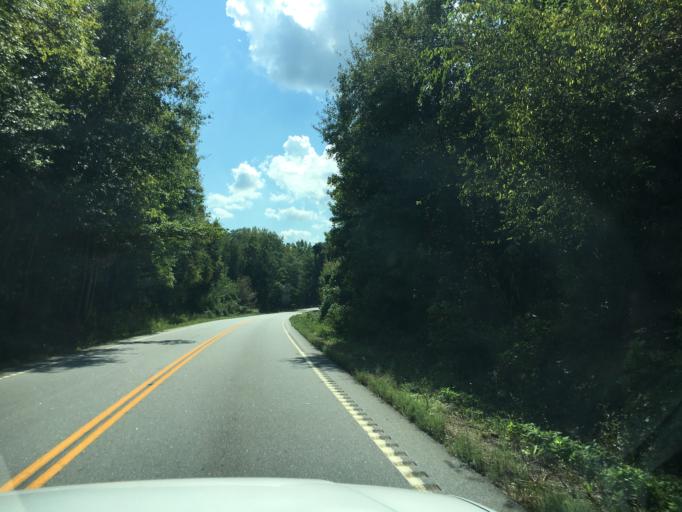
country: US
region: South Carolina
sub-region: Spartanburg County
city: Woodruff
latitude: 34.6906
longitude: -82.0636
